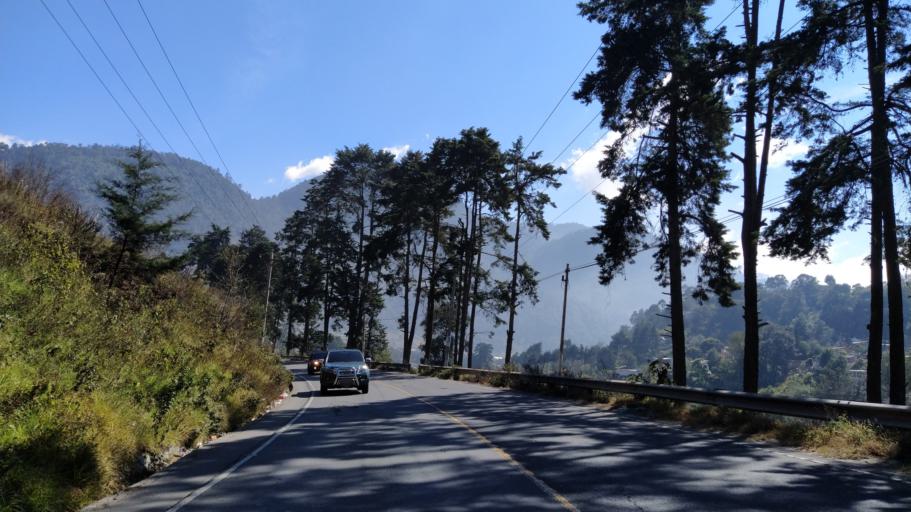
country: GT
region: Quetzaltenango
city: Cantel
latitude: 14.8147
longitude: -91.4529
